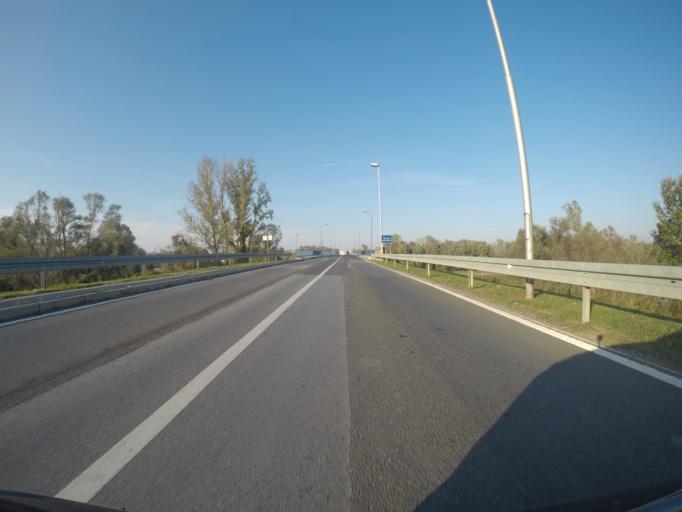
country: HU
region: Somogy
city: Barcs
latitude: 45.9441
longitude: 17.4613
